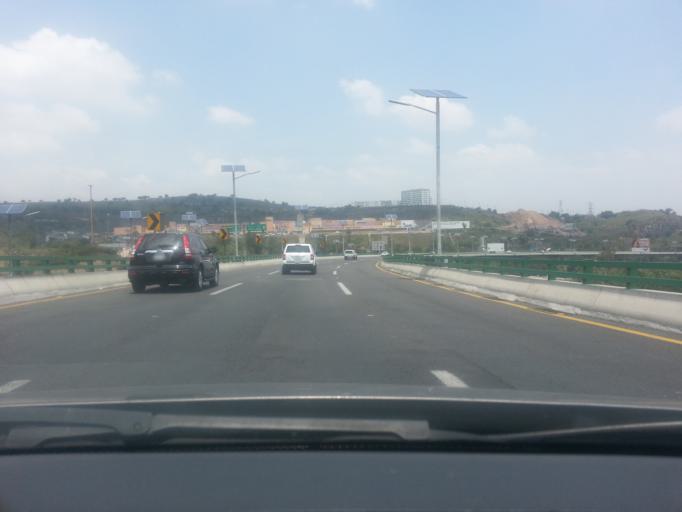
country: MX
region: Mexico
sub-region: Tultitlan
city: Buenavista
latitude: 19.5947
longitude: -99.2017
